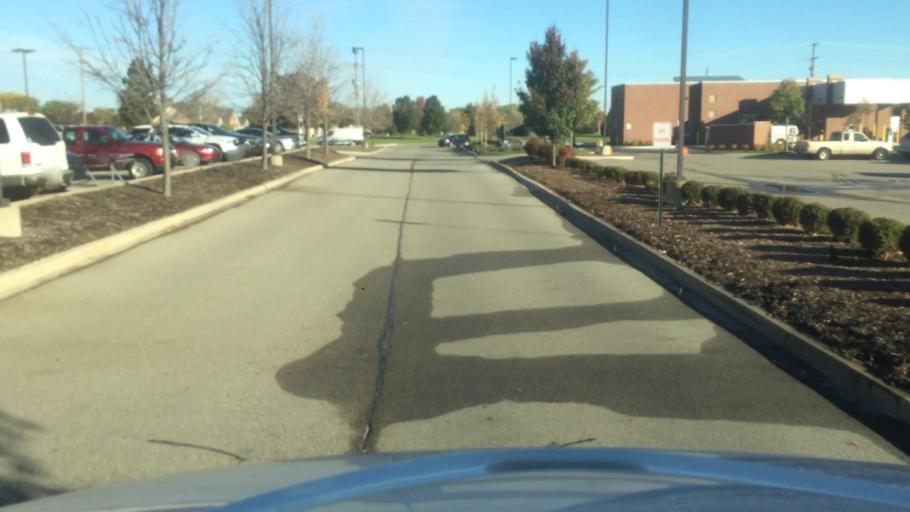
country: US
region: Michigan
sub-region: Macomb County
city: Clinton
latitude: 42.6266
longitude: -82.9423
